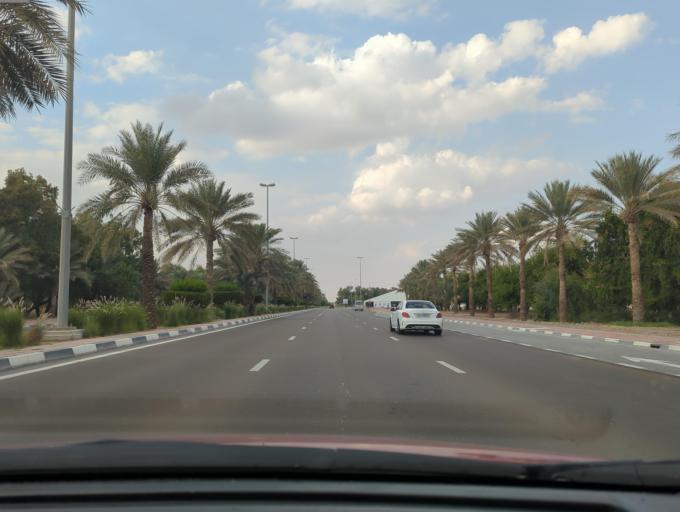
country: AE
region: Abu Dhabi
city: Al Ain
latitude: 24.1813
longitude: 55.6613
